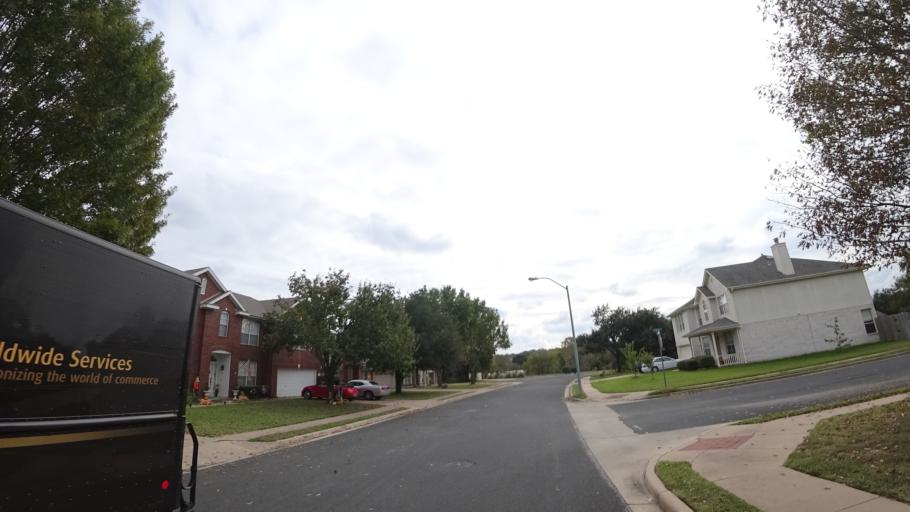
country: US
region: Texas
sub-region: Travis County
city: Wells Branch
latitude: 30.4417
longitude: -97.6745
